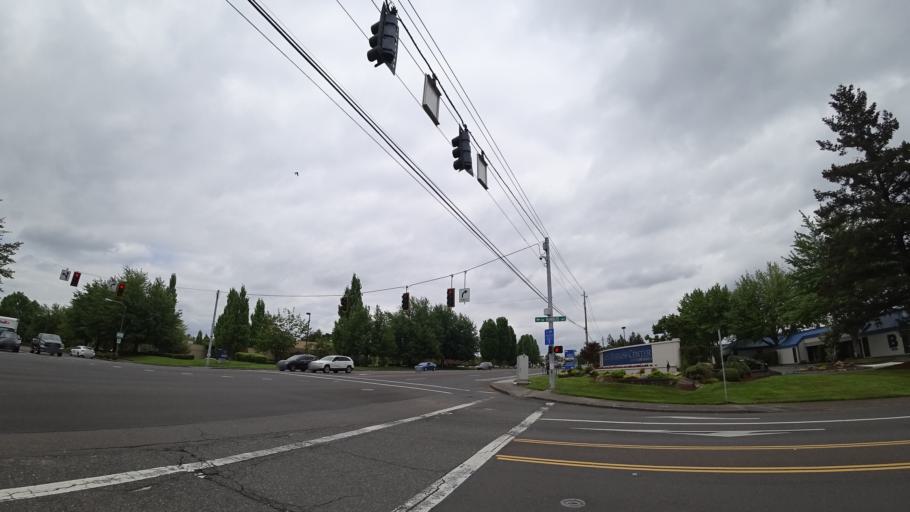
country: US
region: Oregon
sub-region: Washington County
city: Tigard
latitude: 45.4471
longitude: -122.7897
